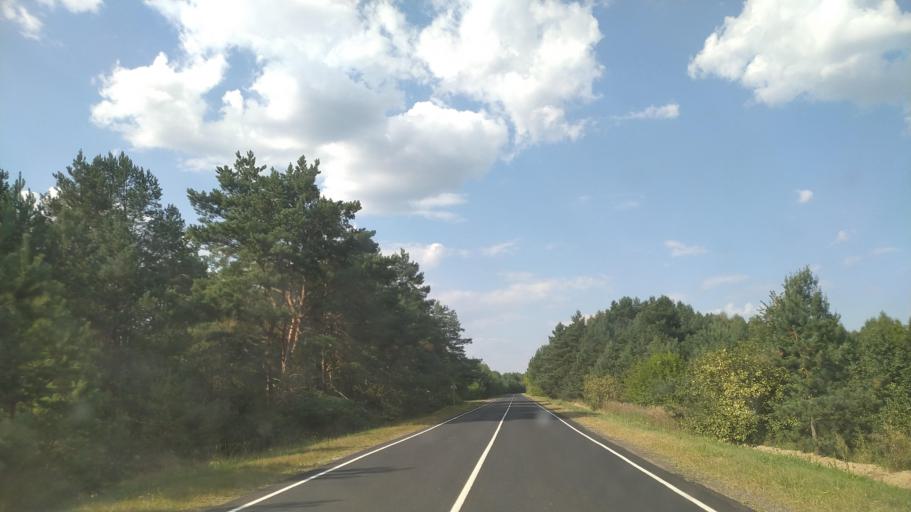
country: BY
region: Brest
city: Drahichyn
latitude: 52.2656
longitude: 25.0728
